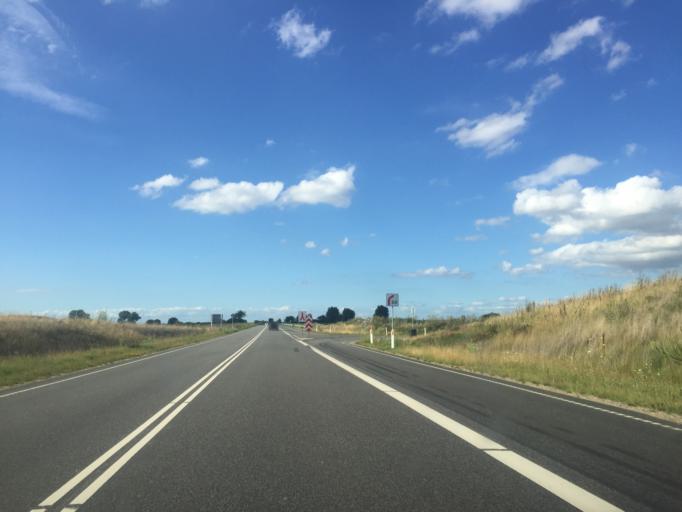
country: DK
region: Zealand
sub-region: Guldborgsund Kommune
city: Nykobing Falster
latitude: 54.7588
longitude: 11.9209
